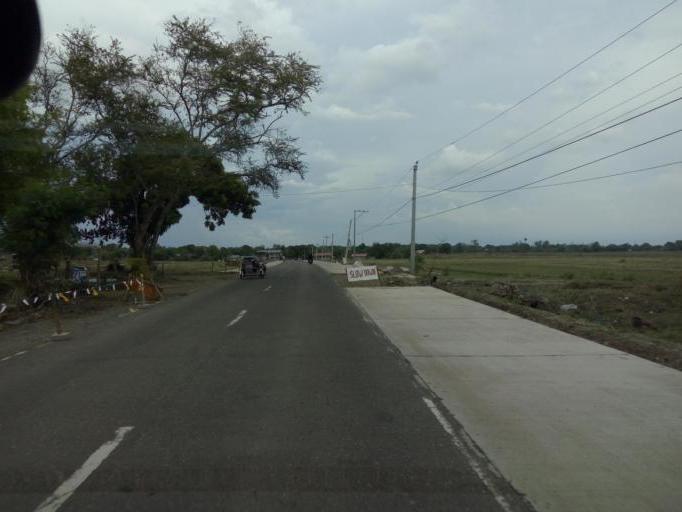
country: PH
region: Central Luzon
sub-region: Province of Nueva Ecija
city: Parista
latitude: 15.8487
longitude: 120.9309
